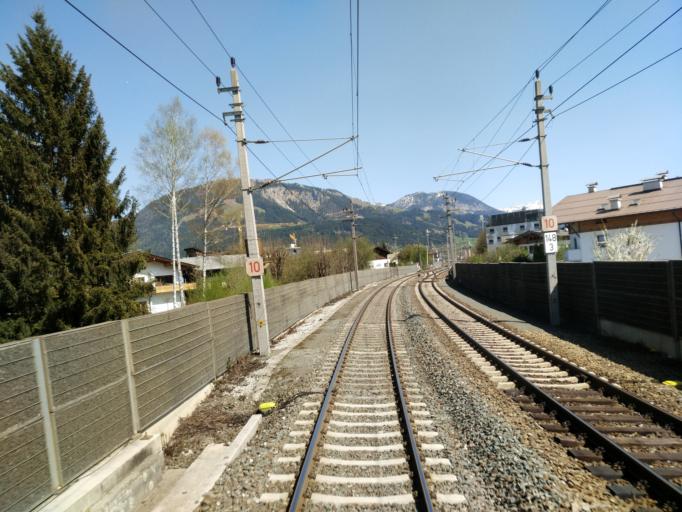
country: AT
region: Tyrol
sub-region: Politischer Bezirk Kitzbuhel
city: Sankt Johann in Tirol
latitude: 47.5199
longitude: 12.4224
